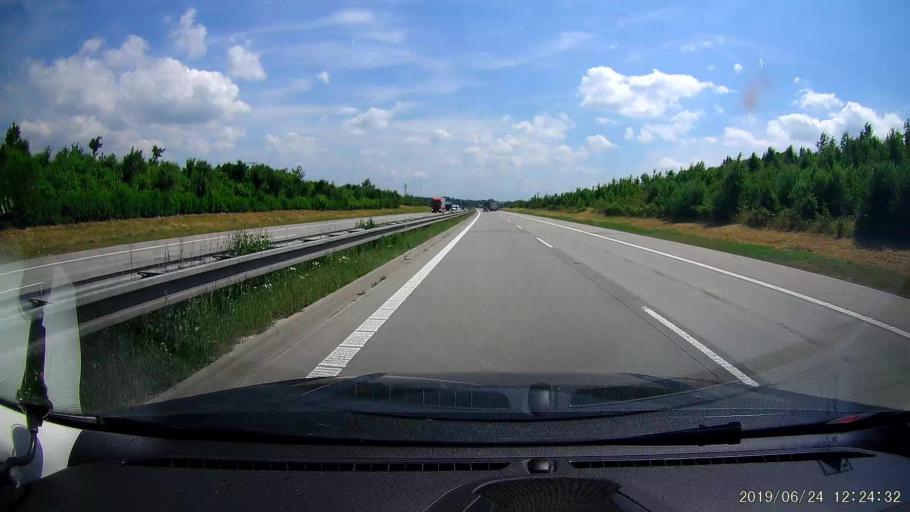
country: CZ
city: Studenka
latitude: 49.7422
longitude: 18.0695
